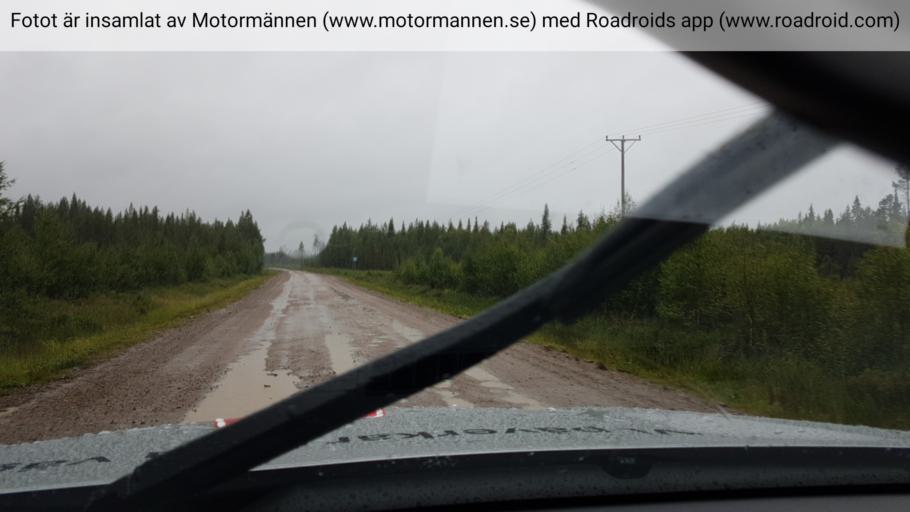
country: SE
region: Norrbotten
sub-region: Jokkmokks Kommun
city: Jokkmokk
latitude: 66.6023
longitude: 19.5334
